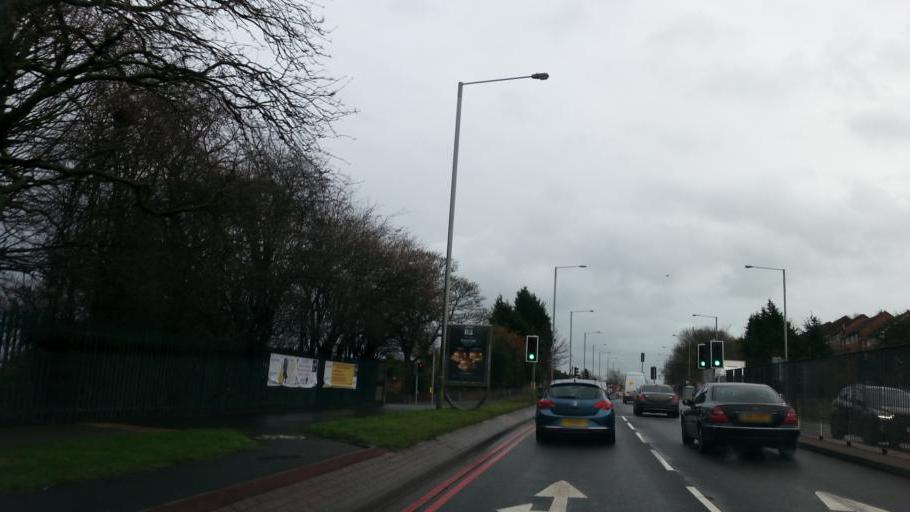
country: GB
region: England
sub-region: Sandwell
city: Oldbury
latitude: 52.5083
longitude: -2.0405
